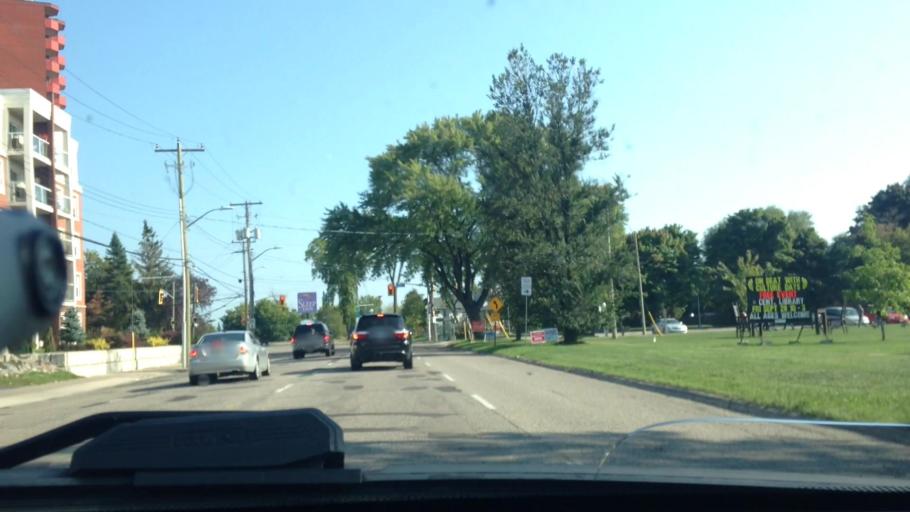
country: CA
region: Ontario
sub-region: Algoma
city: Sault Ste. Marie
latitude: 46.5074
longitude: -84.3301
